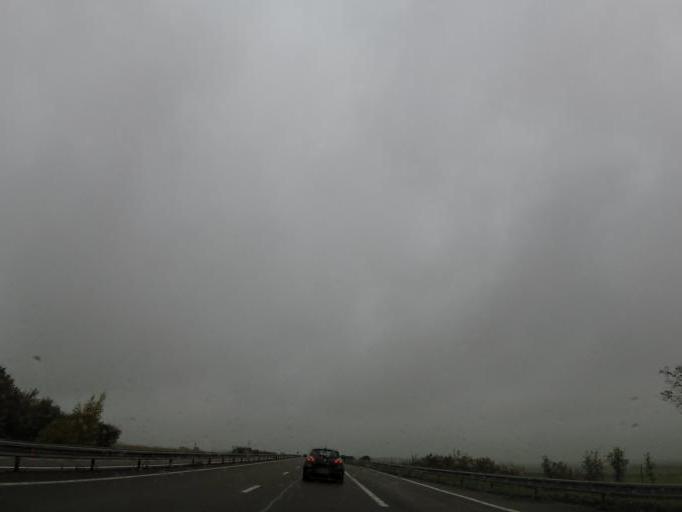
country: FR
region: Champagne-Ardenne
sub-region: Departement de la Marne
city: Courtisols
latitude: 49.0354
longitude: 4.4345
